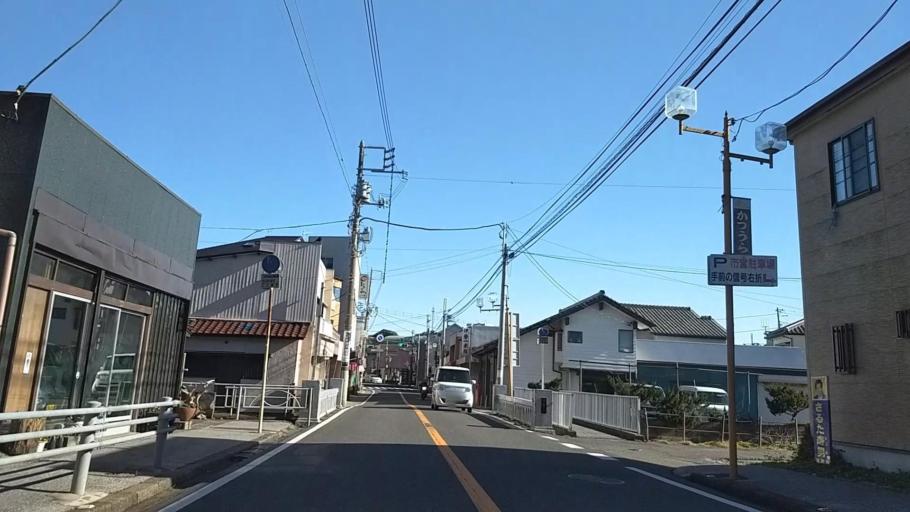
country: JP
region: Chiba
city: Katsuura
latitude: 35.1503
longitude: 140.3122
